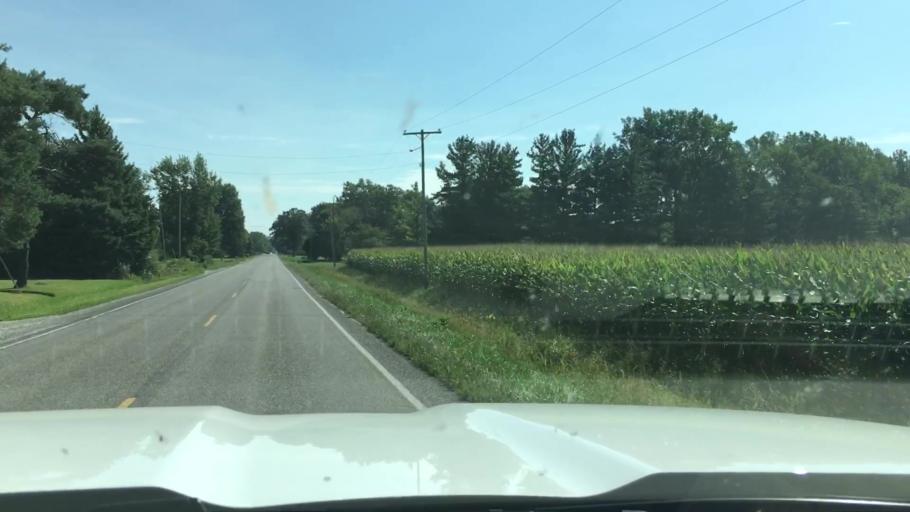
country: US
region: Michigan
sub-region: Saginaw County
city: Freeland
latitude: 43.5252
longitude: -84.1615
